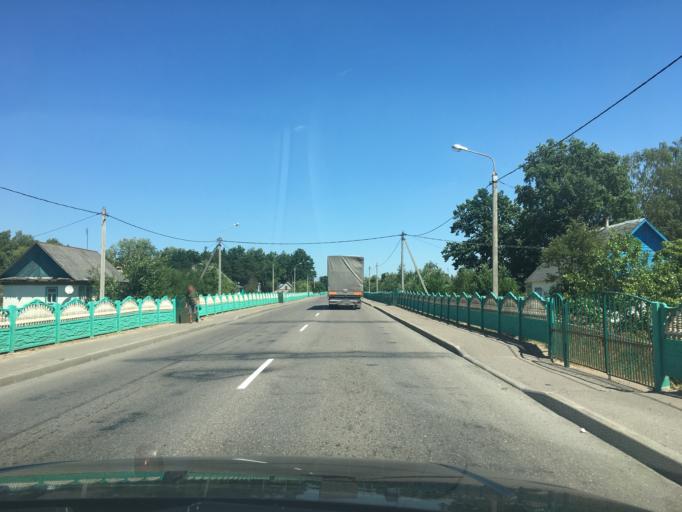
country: BY
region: Grodnenskaya
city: Iwye
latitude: 54.0270
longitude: 25.9219
